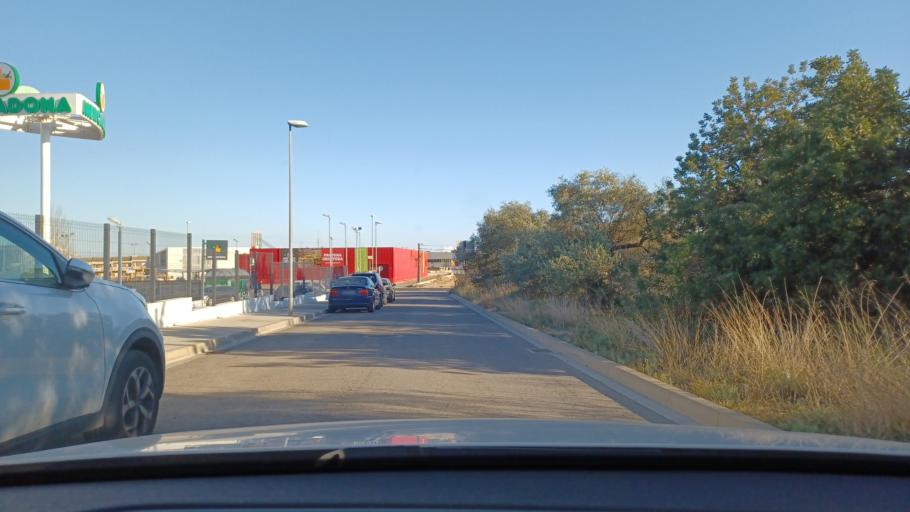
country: ES
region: Catalonia
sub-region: Provincia de Tarragona
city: Amposta
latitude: 40.7060
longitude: 0.5695
